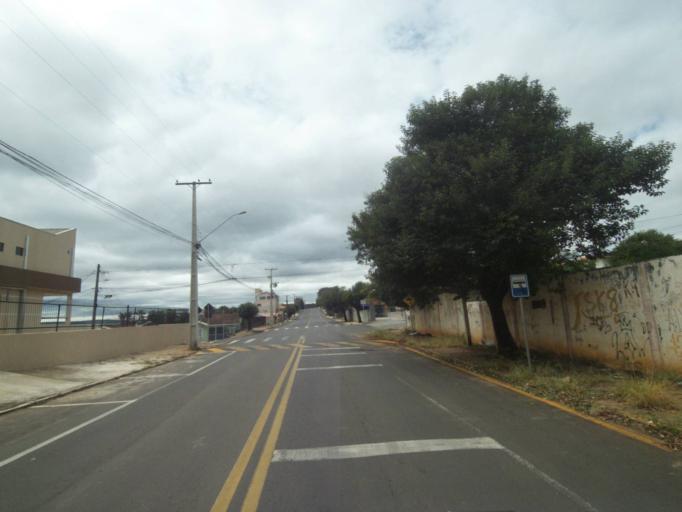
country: BR
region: Parana
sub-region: Telemaco Borba
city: Telemaco Borba
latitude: -24.3391
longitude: -50.6210
